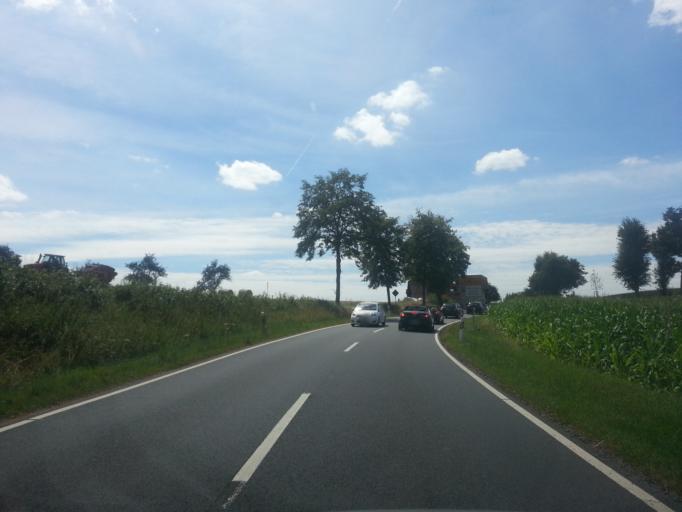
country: DE
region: Hesse
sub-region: Regierungsbezirk Darmstadt
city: Lindenfels
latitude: 49.6828
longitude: 8.8087
